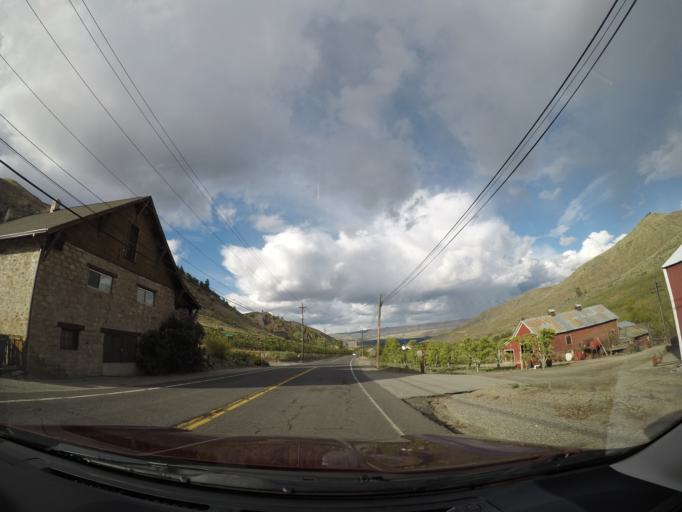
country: US
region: Washington
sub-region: Chelan County
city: South Wenatchee
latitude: 47.3743
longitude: -120.3217
